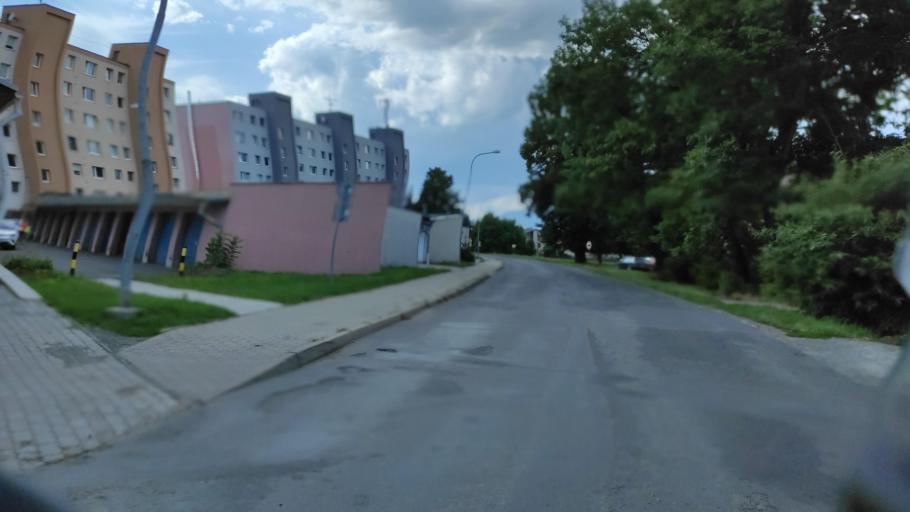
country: SK
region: Zilinsky
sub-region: Okres Liptovsky Mikulas
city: Liptovsky Mikulas
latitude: 49.0852
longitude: 19.5907
